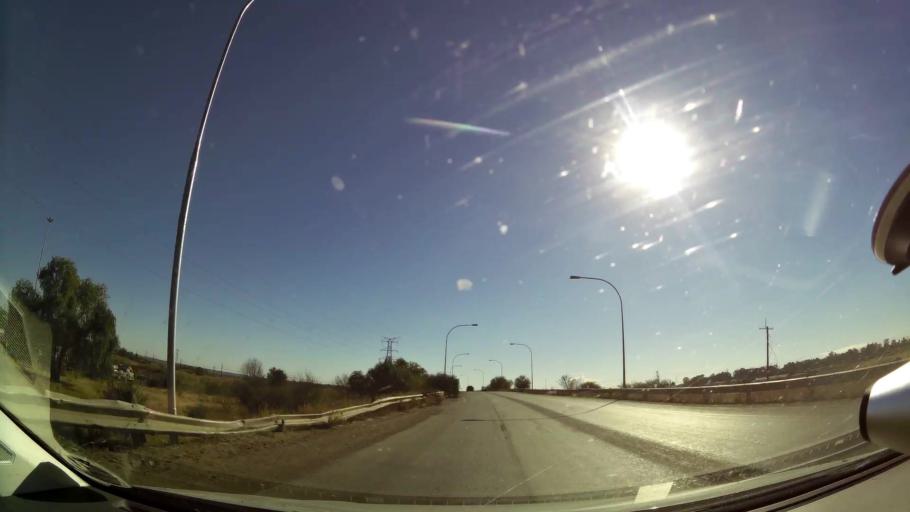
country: ZA
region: Northern Cape
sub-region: Frances Baard District Municipality
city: Kimberley
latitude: -28.7157
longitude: 24.7756
